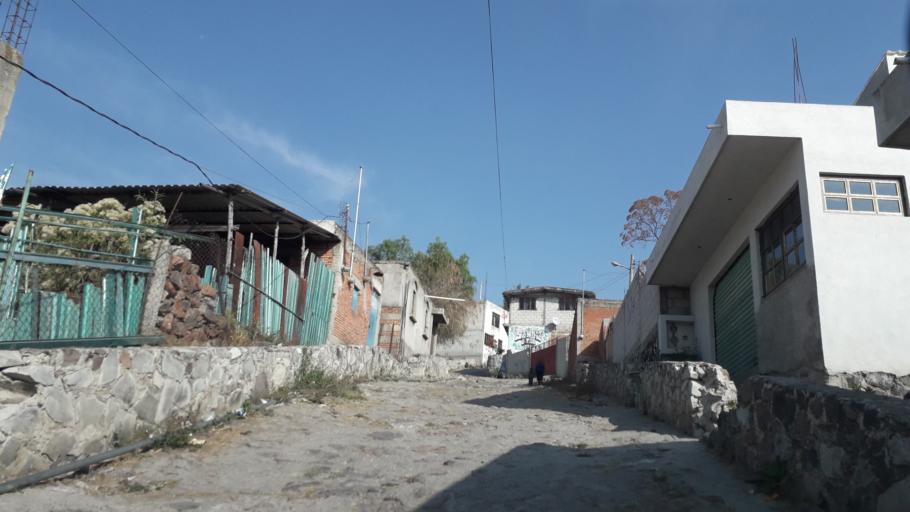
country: MX
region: Puebla
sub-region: Puebla
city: San Andres Azumiatla
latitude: 18.9028
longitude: -98.2537
